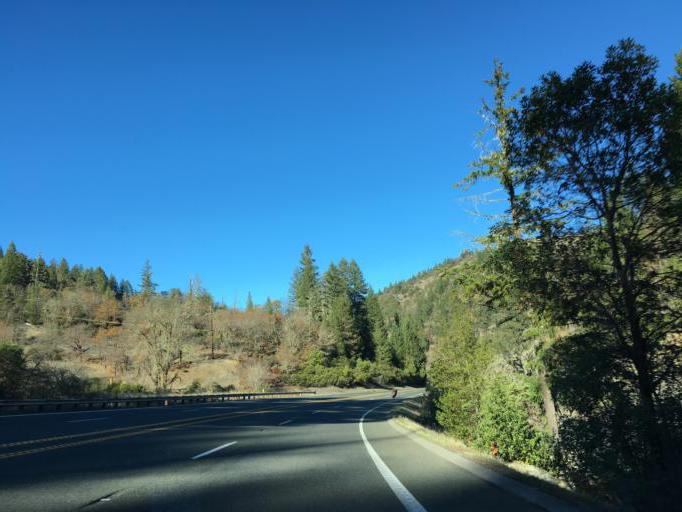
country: US
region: California
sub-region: Mendocino County
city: Laytonville
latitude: 39.5988
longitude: -123.4546
